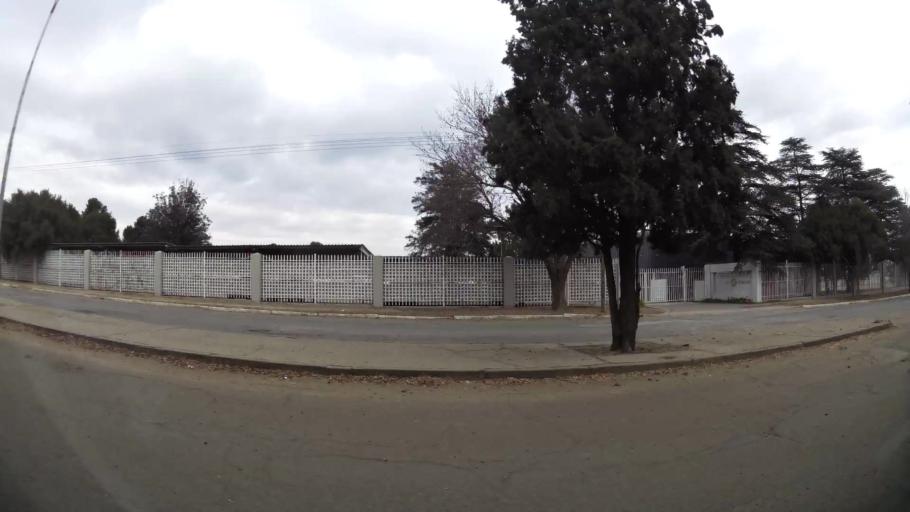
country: ZA
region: Orange Free State
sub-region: Fezile Dabi District Municipality
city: Kroonstad
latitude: -27.6778
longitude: 27.2329
